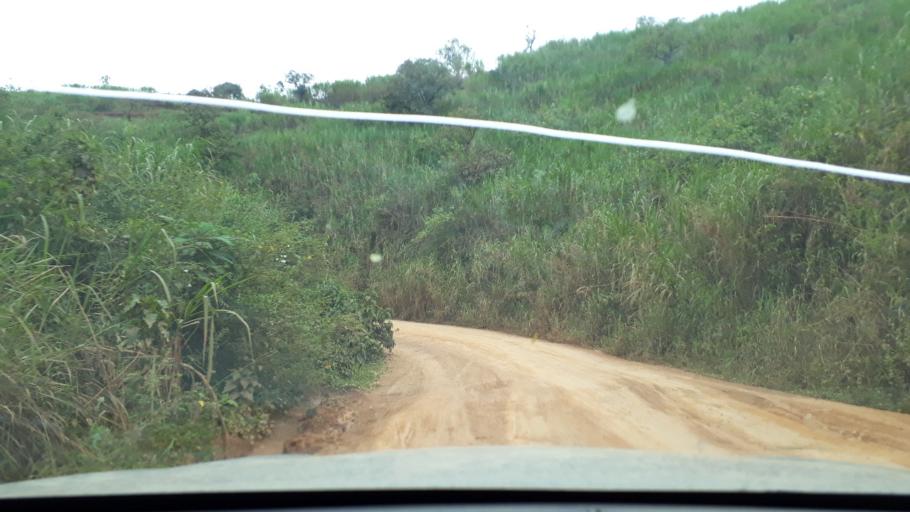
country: CD
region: Eastern Province
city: Bunia
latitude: 1.8065
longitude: 30.4134
